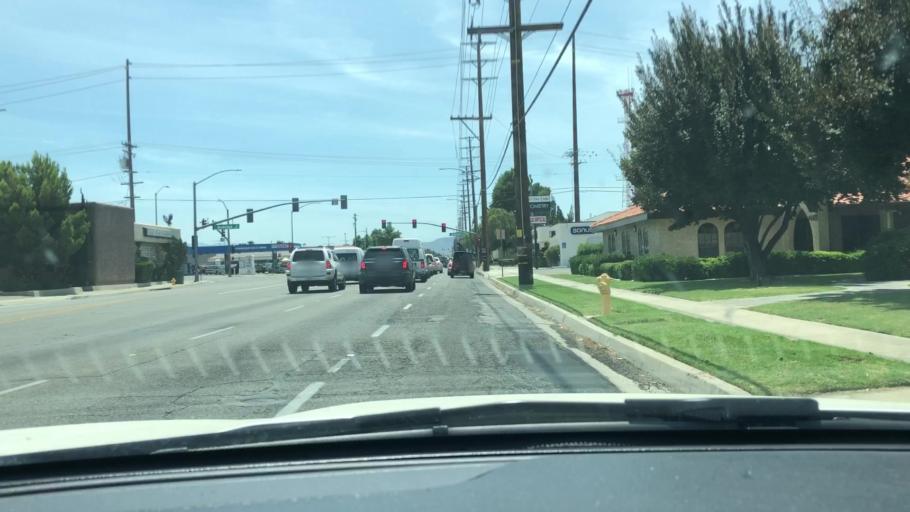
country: US
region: California
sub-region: Los Angeles County
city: Lancaster
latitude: 34.6903
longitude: -118.1482
